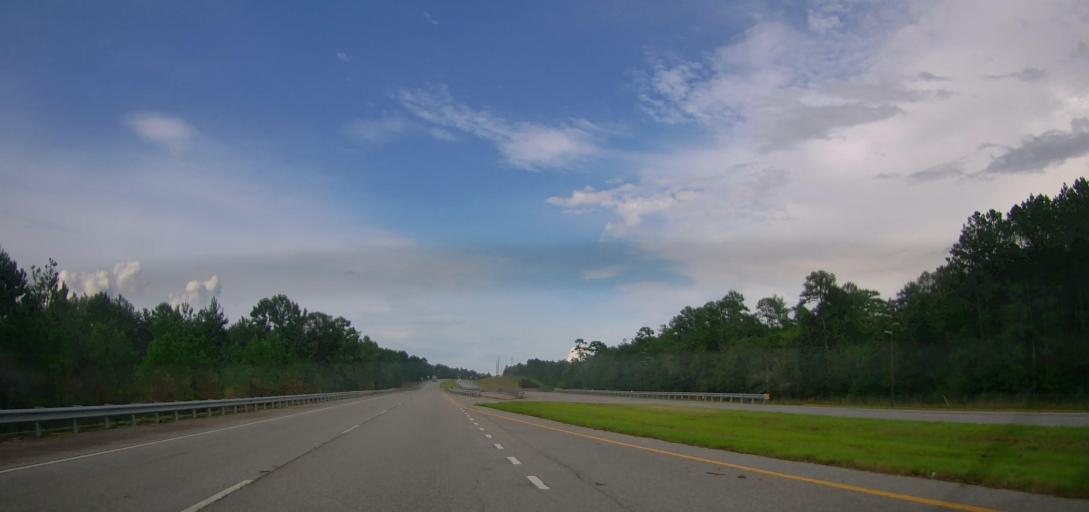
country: US
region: Georgia
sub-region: Wayne County
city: Jesup
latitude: 31.4631
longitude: -82.0496
